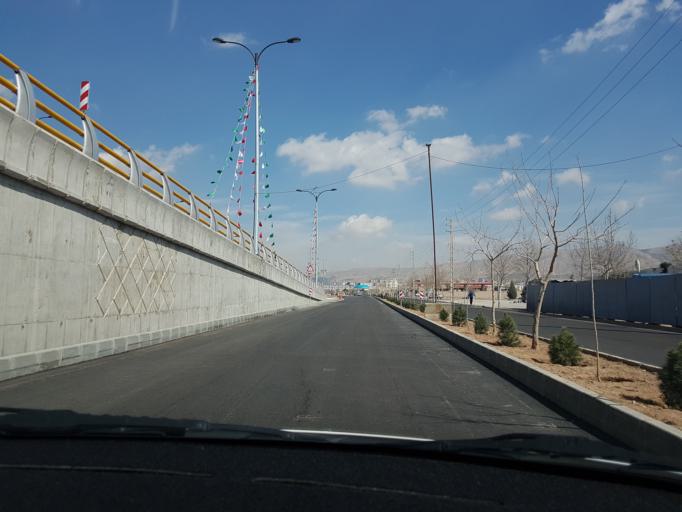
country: IR
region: Fars
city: Shiraz
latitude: 29.6168
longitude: 52.4688
